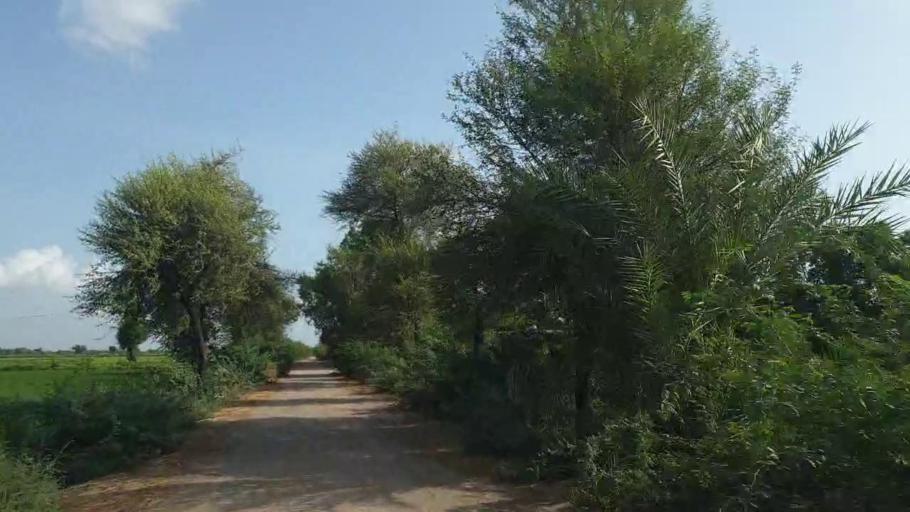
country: PK
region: Sindh
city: Kadhan
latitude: 24.6231
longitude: 69.0959
